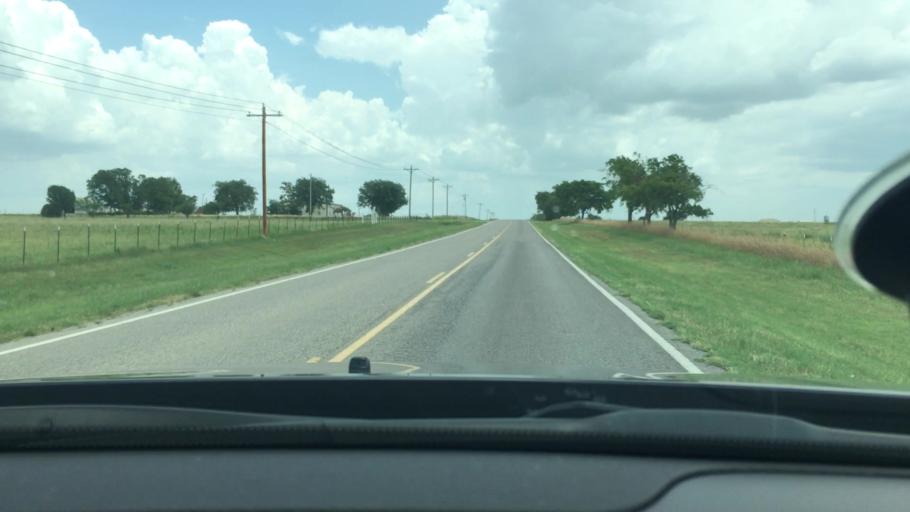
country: US
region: Oklahoma
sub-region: Love County
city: Marietta
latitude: 33.9403
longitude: -97.0631
